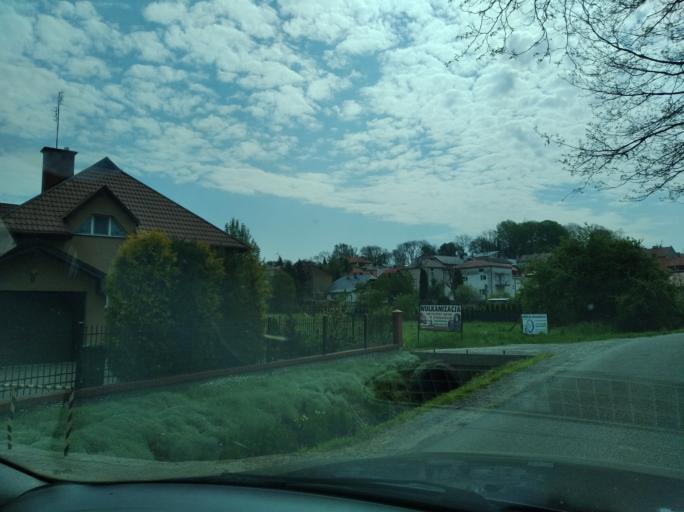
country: PL
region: Subcarpathian Voivodeship
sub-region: Powiat jaroslawski
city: Jaroslaw
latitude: 50.0149
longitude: 22.6649
